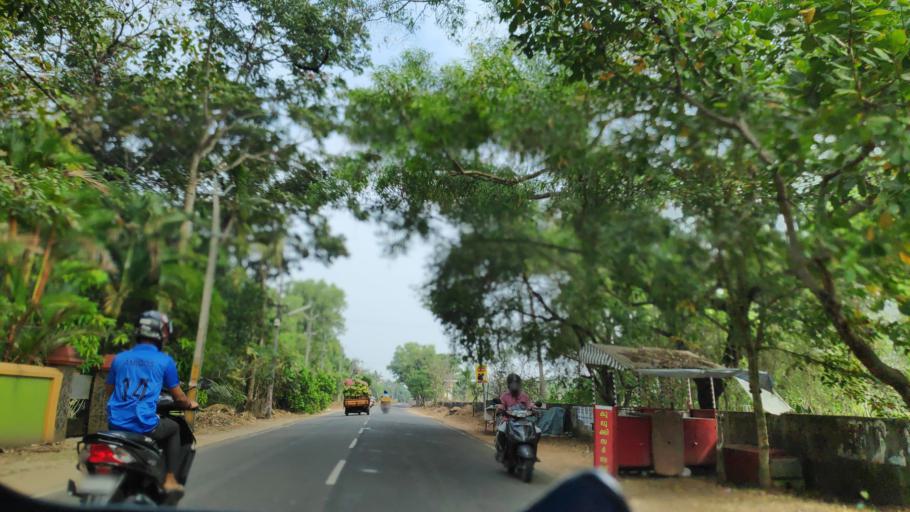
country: IN
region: Kerala
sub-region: Kottayam
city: Vaikam
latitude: 9.7556
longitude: 76.3630
